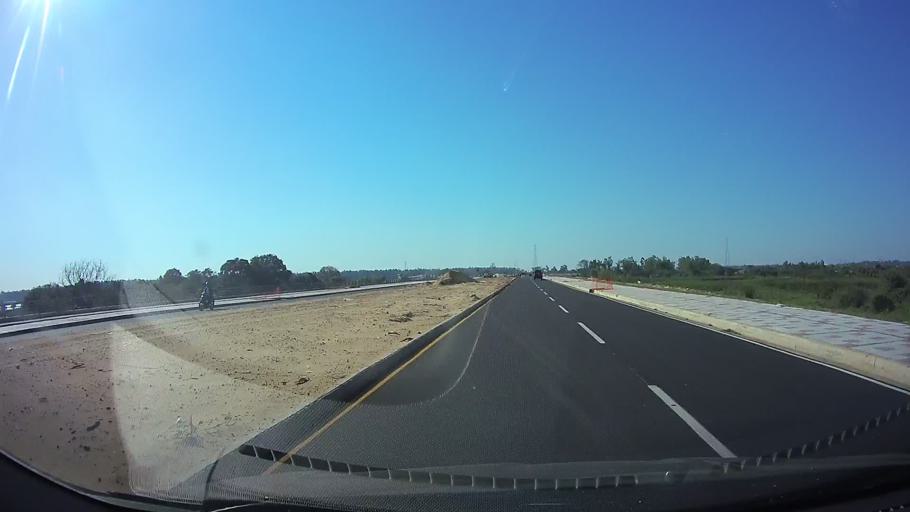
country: PY
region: Asuncion
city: Asuncion
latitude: -25.2552
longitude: -57.6071
